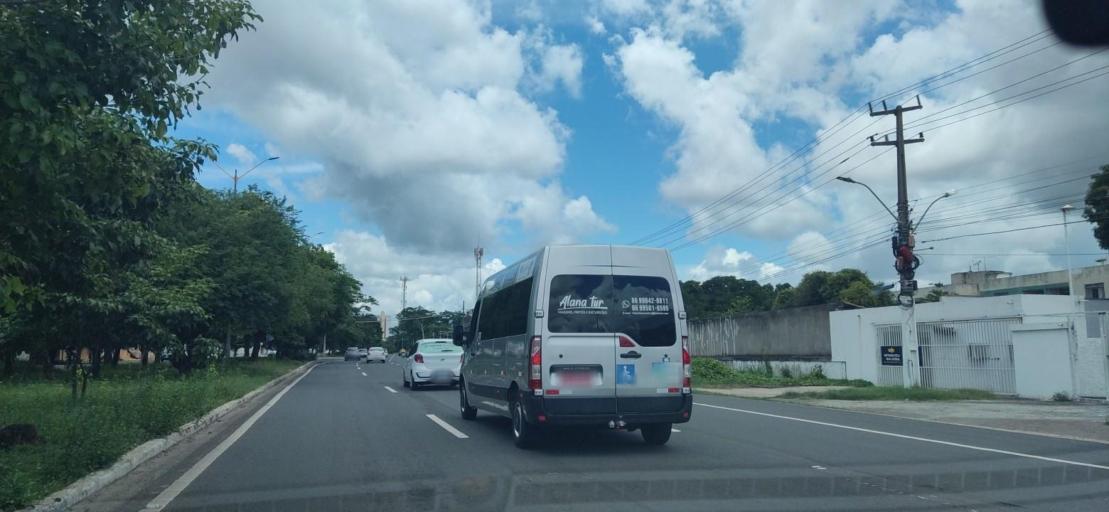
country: BR
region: Piaui
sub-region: Teresina
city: Teresina
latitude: -5.0816
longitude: -42.7728
